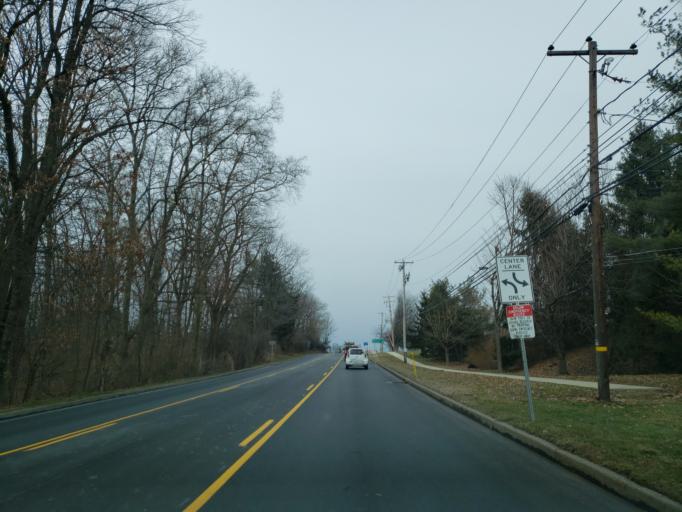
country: US
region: Pennsylvania
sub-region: Lehigh County
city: Dorneyville
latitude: 40.5953
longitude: -75.5270
